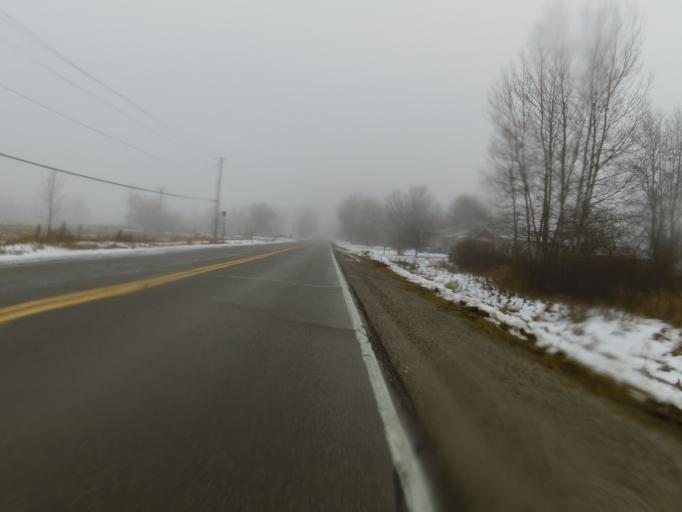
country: CA
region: Ontario
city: Perth
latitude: 44.8435
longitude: -76.3657
